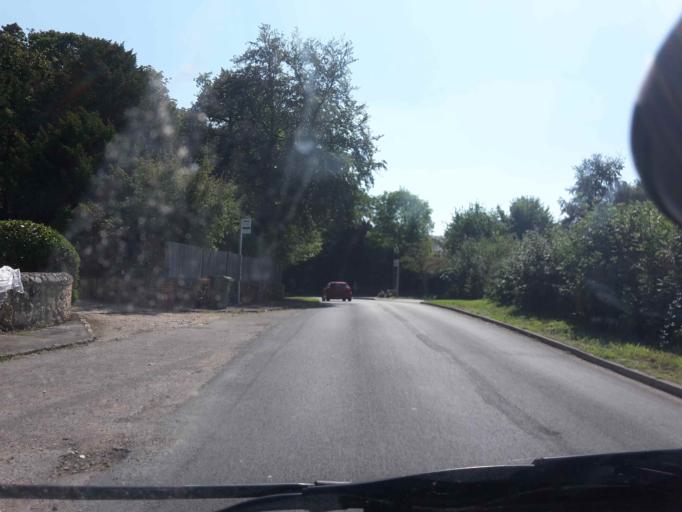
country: GB
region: England
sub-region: Surrey
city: Chilworth
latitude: 51.2218
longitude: -0.4708
